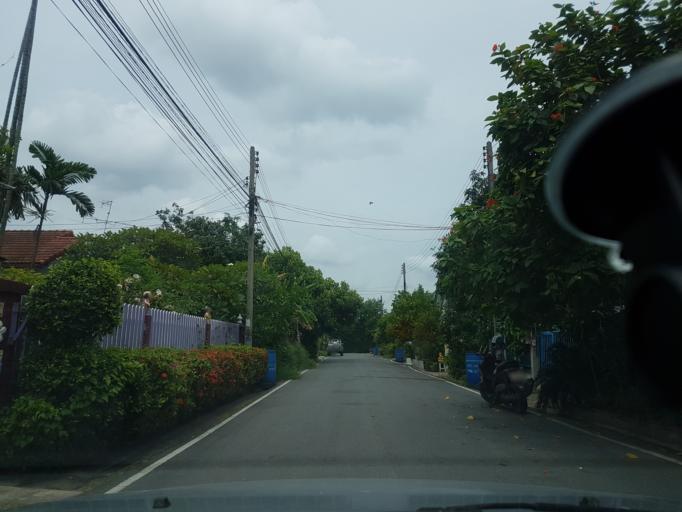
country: TH
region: Lop Buri
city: Lop Buri
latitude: 14.7707
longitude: 100.6959
